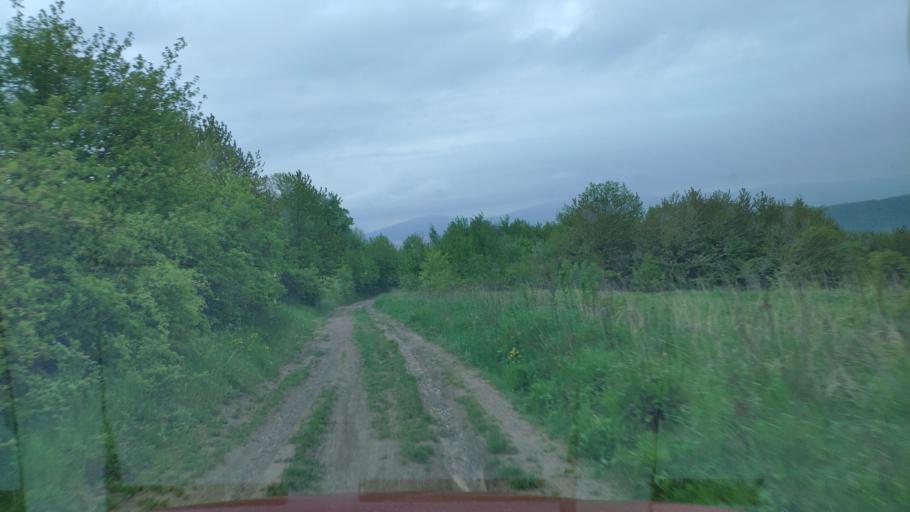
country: SK
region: Kosicky
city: Kosice
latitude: 48.7679
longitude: 21.2073
